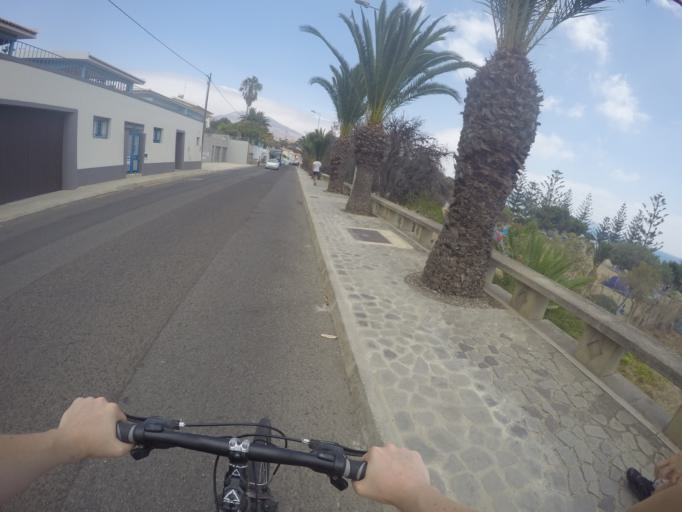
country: PT
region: Madeira
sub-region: Porto Santo
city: Vila de Porto Santo
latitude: 33.0541
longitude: -16.3506
